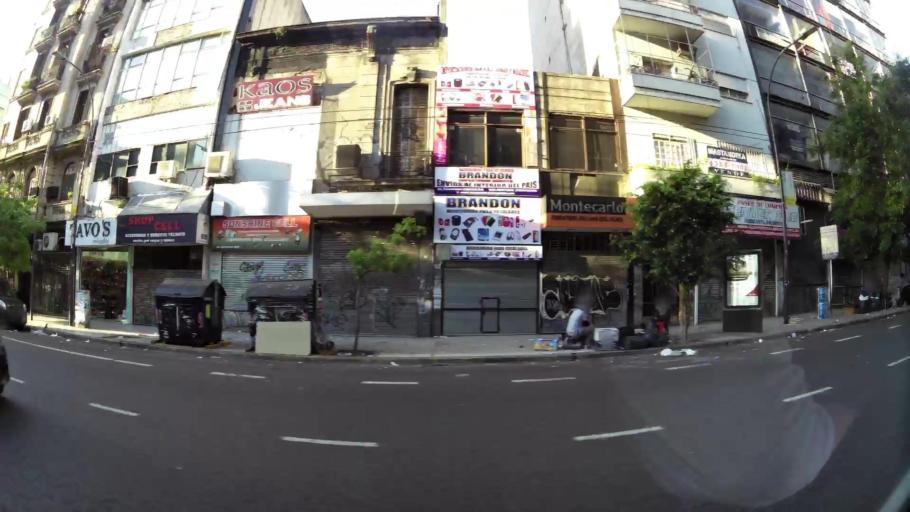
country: AR
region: Buenos Aires F.D.
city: Buenos Aires
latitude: -34.6045
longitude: -58.4019
